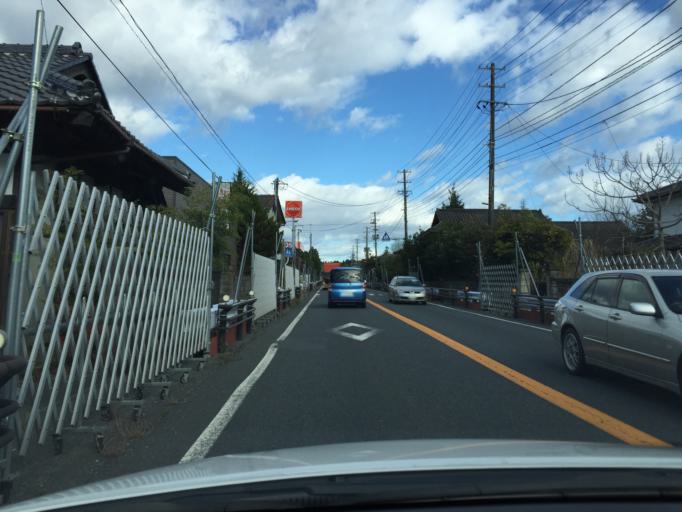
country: JP
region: Fukushima
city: Namie
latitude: 37.3822
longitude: 141.0087
